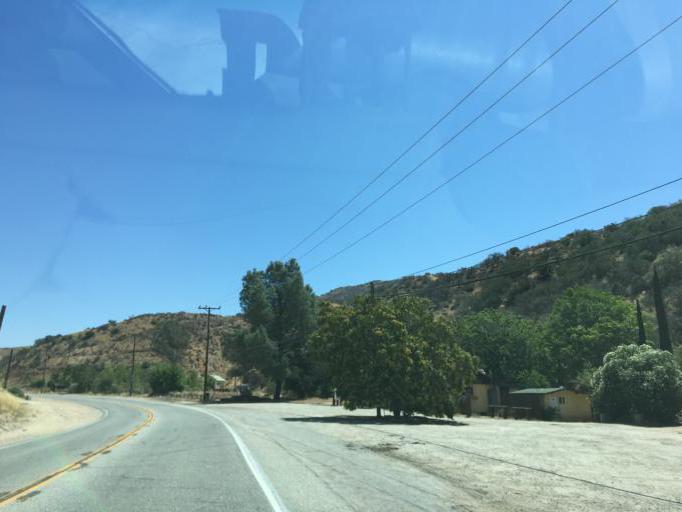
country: US
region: California
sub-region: Los Angeles County
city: Agua Dulce
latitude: 34.5023
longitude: -118.3788
